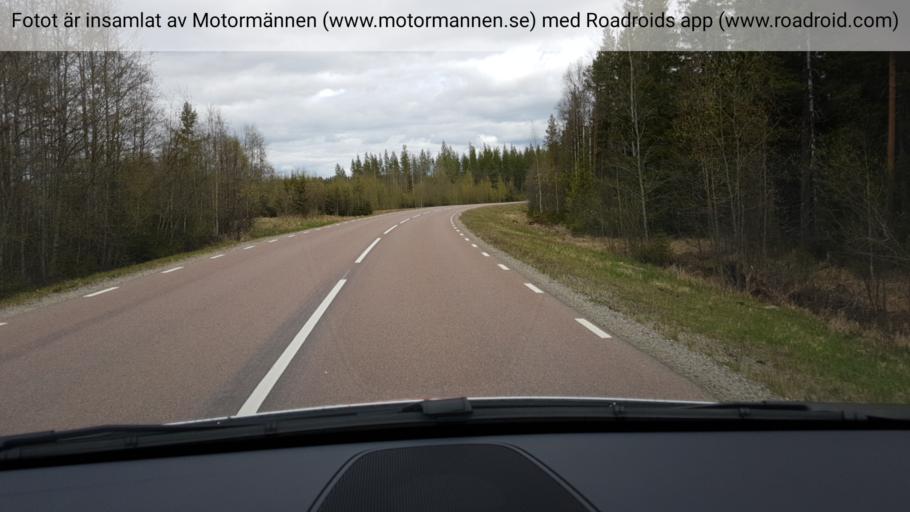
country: SE
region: Jaemtland
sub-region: Braecke Kommun
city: Braecke
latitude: 62.7495
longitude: 15.2452
